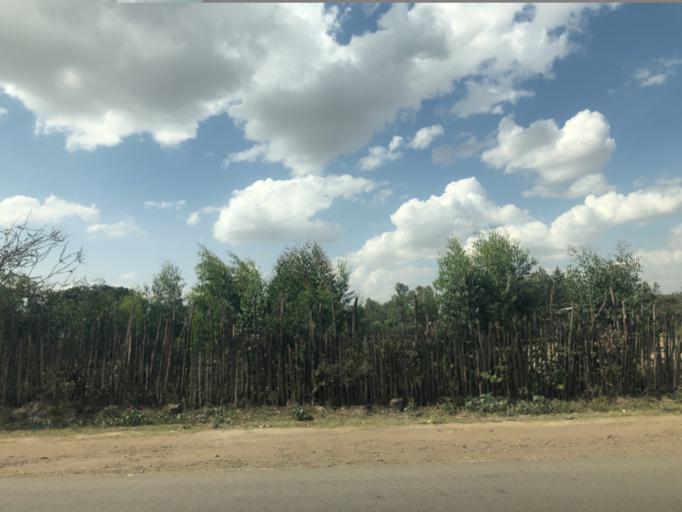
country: ET
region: Southern Nations, Nationalities, and People's Region
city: K'olito
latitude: 7.3045
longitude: 38.0892
